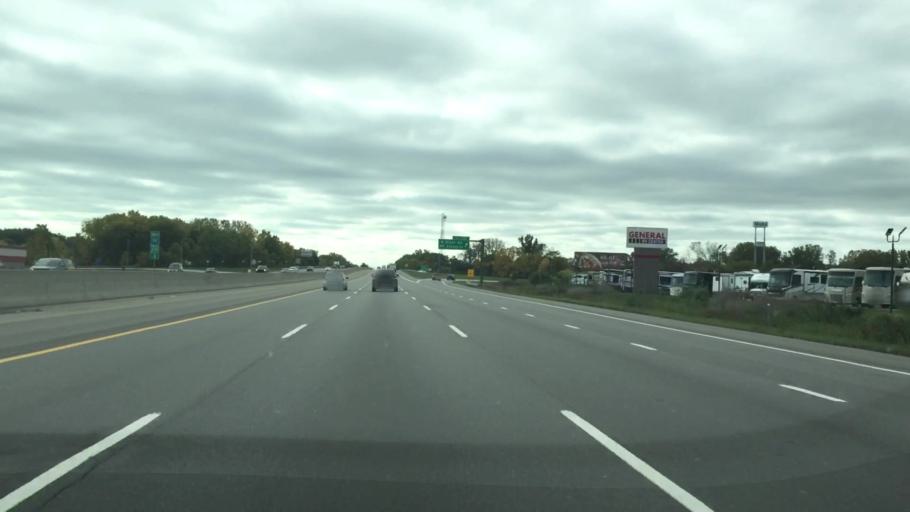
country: US
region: Michigan
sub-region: Macomb County
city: Mount Clemens
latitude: 42.5960
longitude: -82.8571
